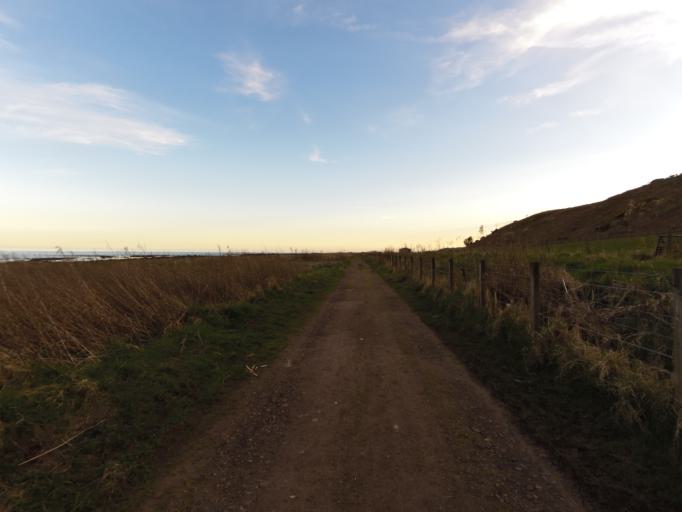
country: GB
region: Scotland
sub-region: Aberdeenshire
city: Inverbervie
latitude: 56.8240
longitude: -2.2930
